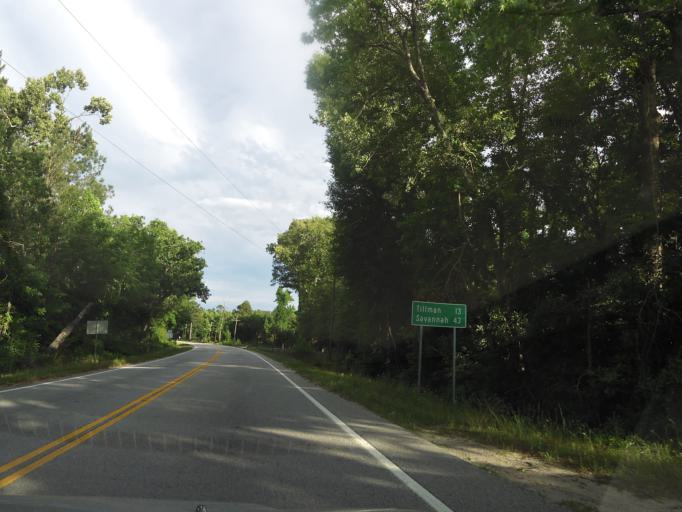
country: US
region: South Carolina
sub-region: Hampton County
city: Estill
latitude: 32.6064
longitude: -81.2425
